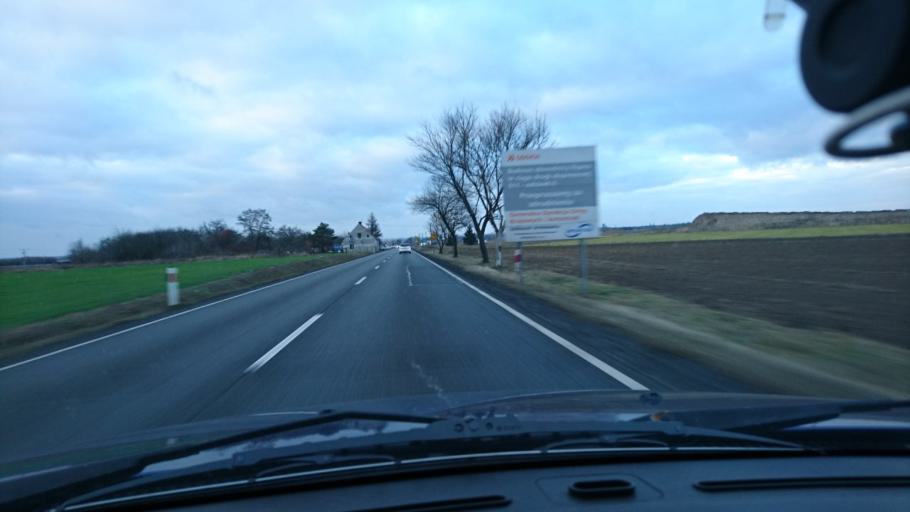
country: PL
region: Greater Poland Voivodeship
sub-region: Powiat kepinski
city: Baranow
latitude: 51.2533
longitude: 18.0128
